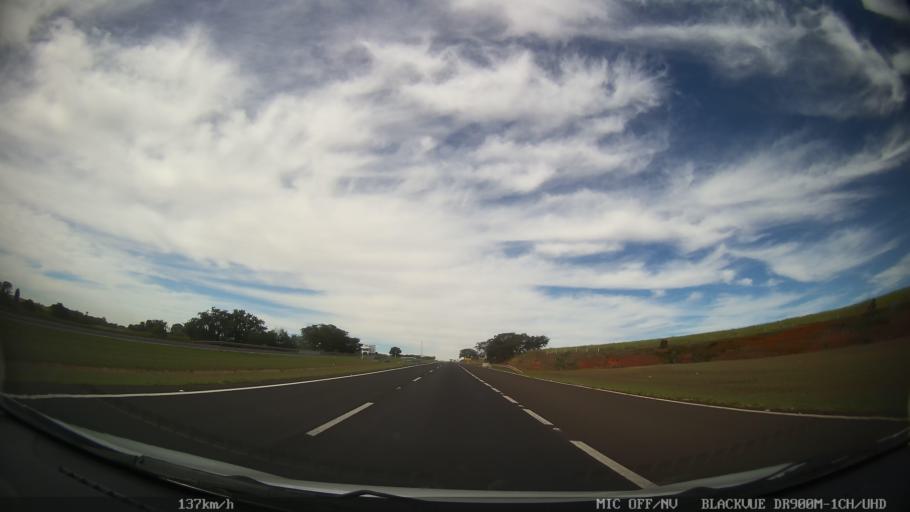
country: BR
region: Sao Paulo
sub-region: Taquaritinga
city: Taquaritinga
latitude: -21.4950
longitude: -48.5705
